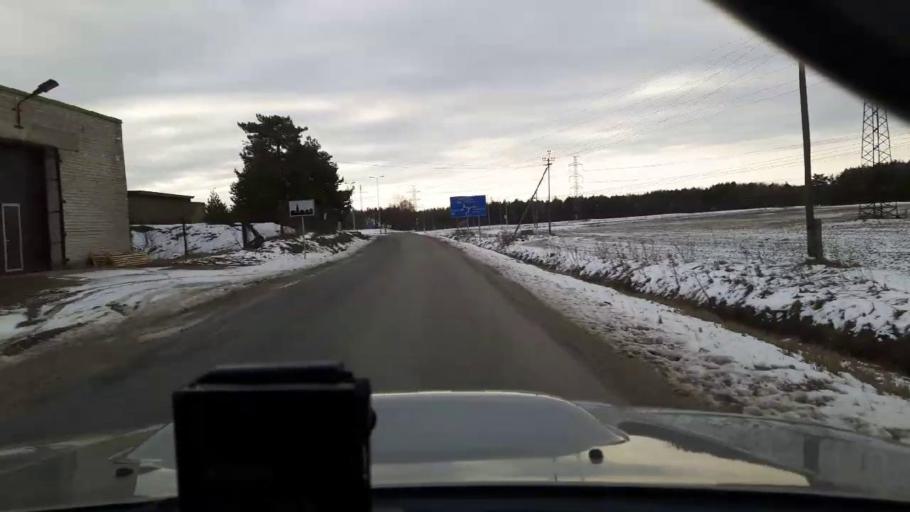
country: EE
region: Harju
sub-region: Saue vald
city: Laagri
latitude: 59.3483
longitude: 24.5993
